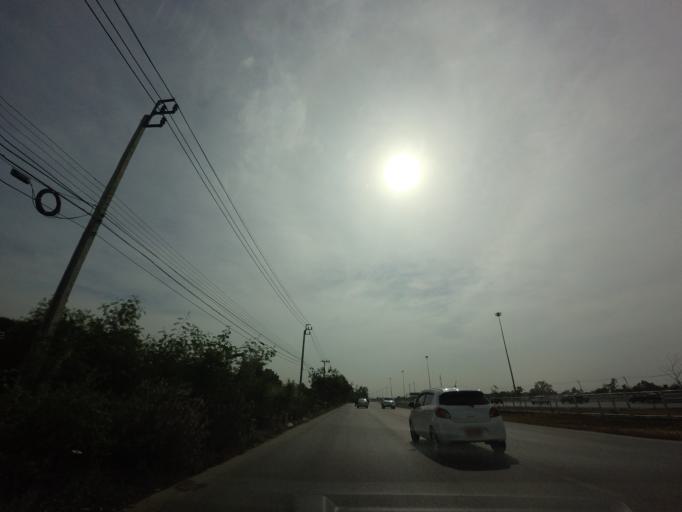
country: TH
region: Bangkok
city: Sai Mai
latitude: 13.8923
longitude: 100.6912
